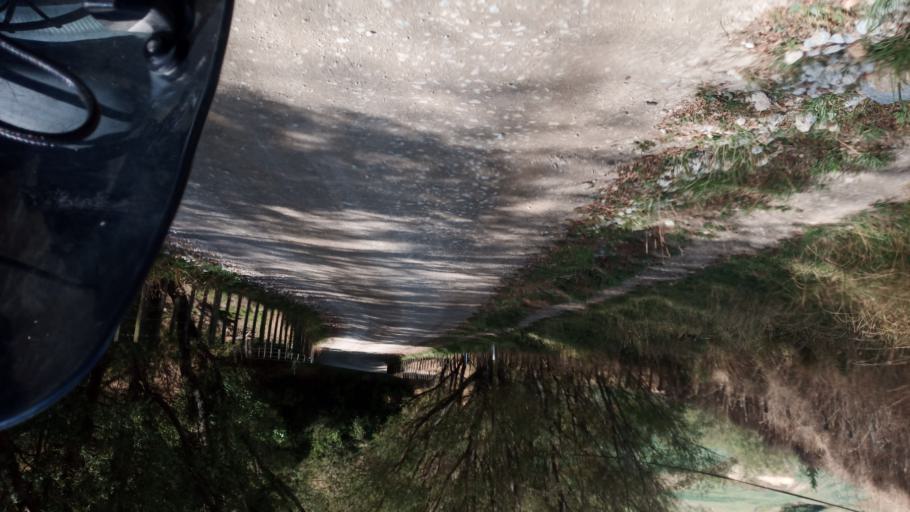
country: NZ
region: Hawke's Bay
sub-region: Wairoa District
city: Wairoa
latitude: -38.6058
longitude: 177.4556
